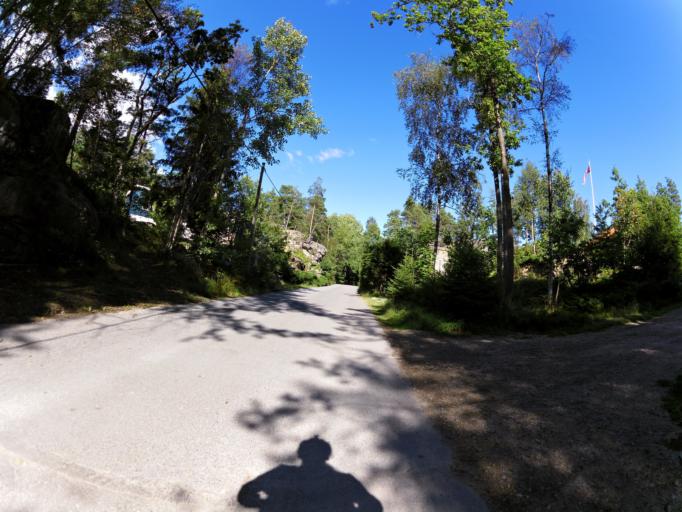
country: NO
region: Ostfold
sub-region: Fredrikstad
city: Fredrikstad
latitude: 59.1729
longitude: 10.8362
